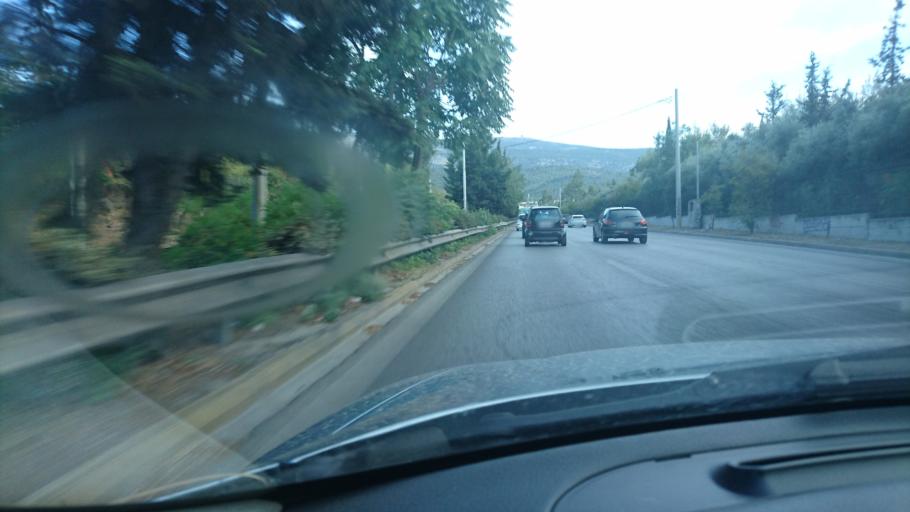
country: GR
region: Attica
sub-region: Nomos Attikis
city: Zografos
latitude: 37.9804
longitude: 23.7858
